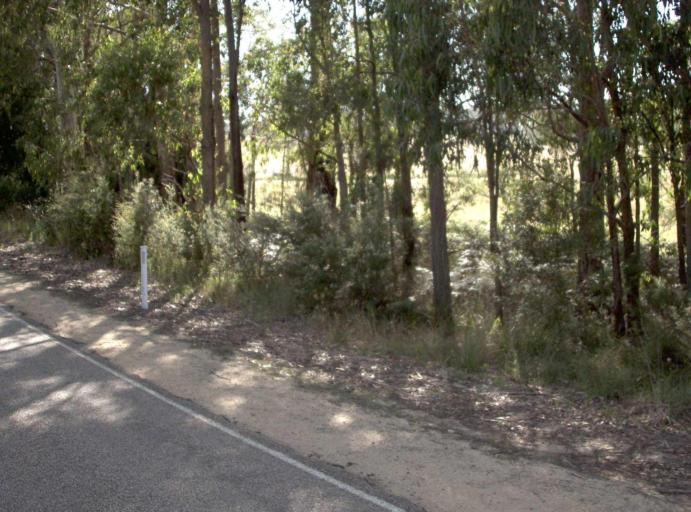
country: AU
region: Victoria
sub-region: East Gippsland
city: Lakes Entrance
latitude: -37.5345
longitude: 148.1498
